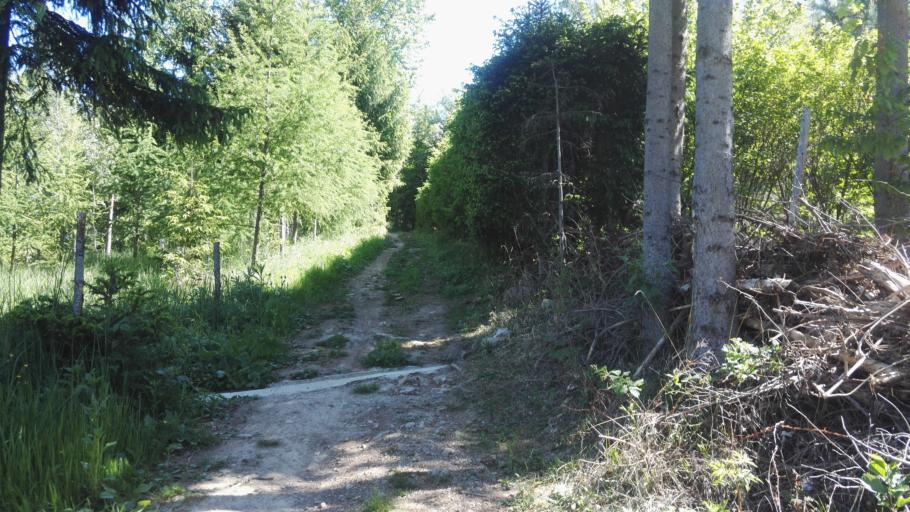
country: AT
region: Styria
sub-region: Politischer Bezirk Graz-Umgebung
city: Thal
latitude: 47.0777
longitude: 15.3709
